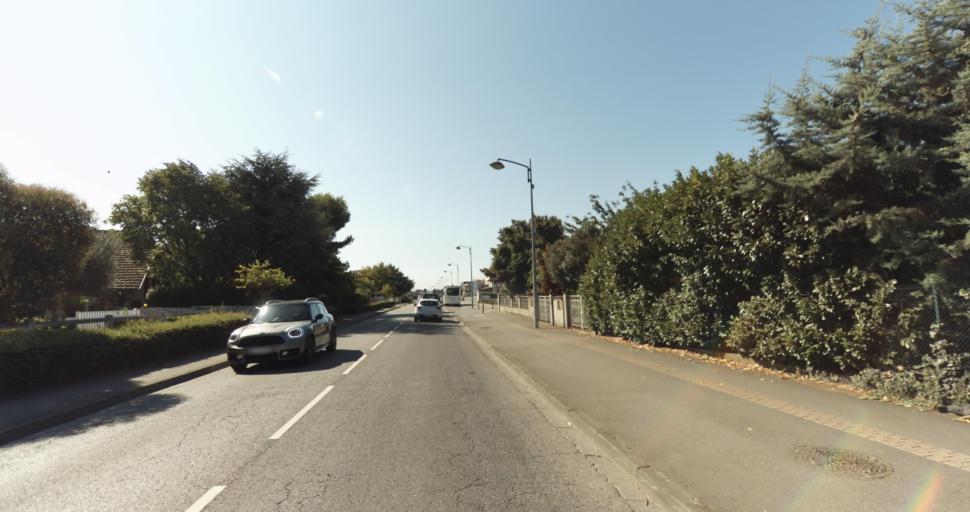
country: FR
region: Midi-Pyrenees
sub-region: Departement de la Haute-Garonne
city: L'Union
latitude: 43.6530
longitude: 1.4709
